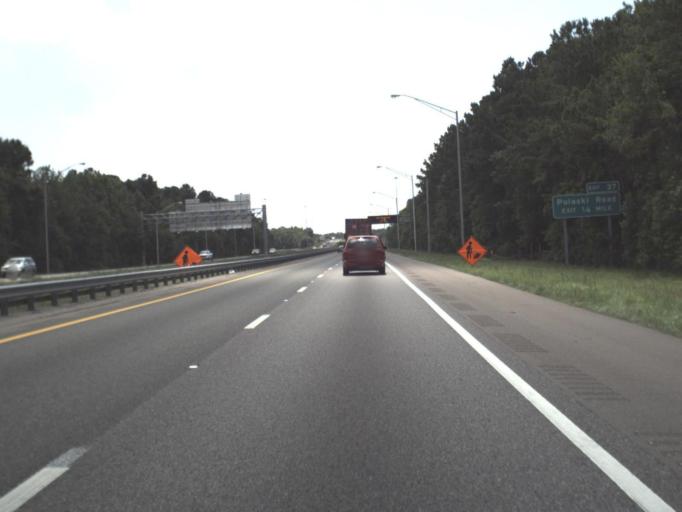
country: US
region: Florida
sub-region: Duval County
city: Jacksonville
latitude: 30.4540
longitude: -81.6223
